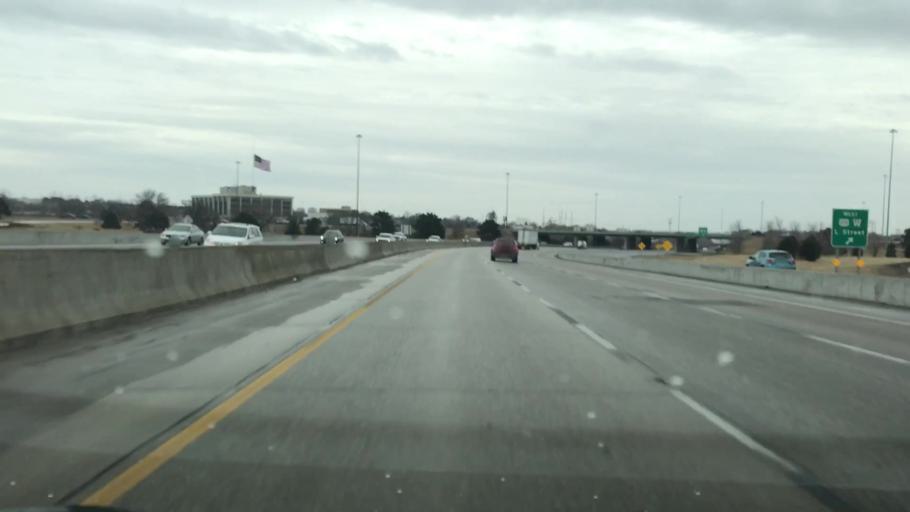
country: US
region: Nebraska
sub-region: Douglas County
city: Ralston
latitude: 41.2154
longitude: -96.0909
